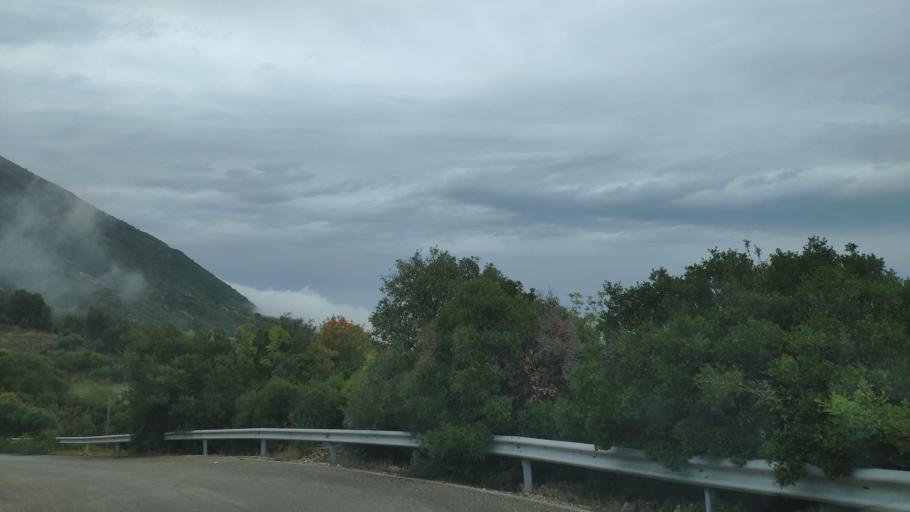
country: GR
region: Epirus
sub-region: Nomos Thesprotias
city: Paramythia
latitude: 39.4575
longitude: 20.6705
